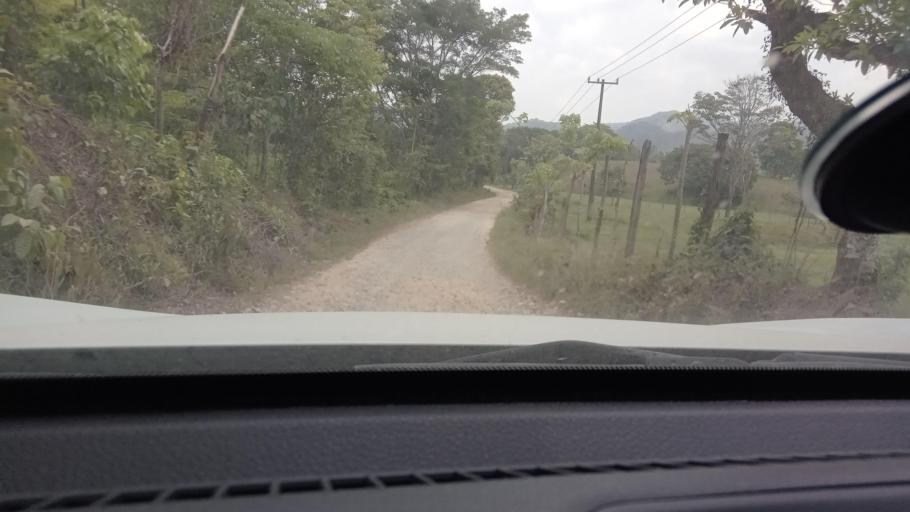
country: MX
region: Tabasco
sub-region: Huimanguillo
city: Francisco Rueda
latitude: 17.5195
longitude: -93.8870
